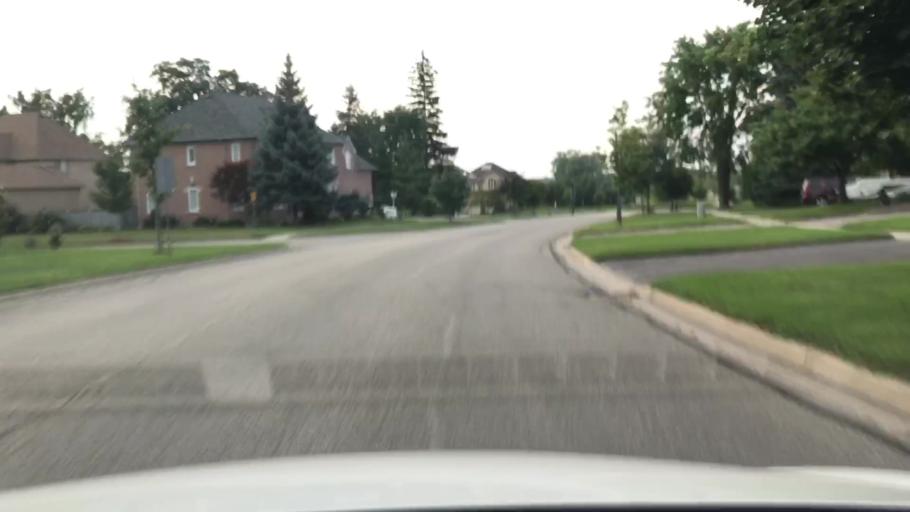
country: CA
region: Ontario
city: Newmarket
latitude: 44.0399
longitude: -79.4384
